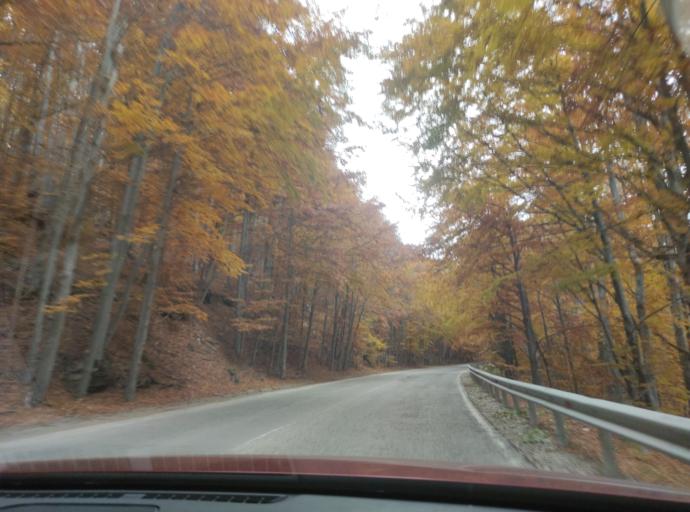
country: BG
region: Montana
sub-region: Obshtina Berkovitsa
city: Berkovitsa
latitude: 43.1156
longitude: 23.1123
